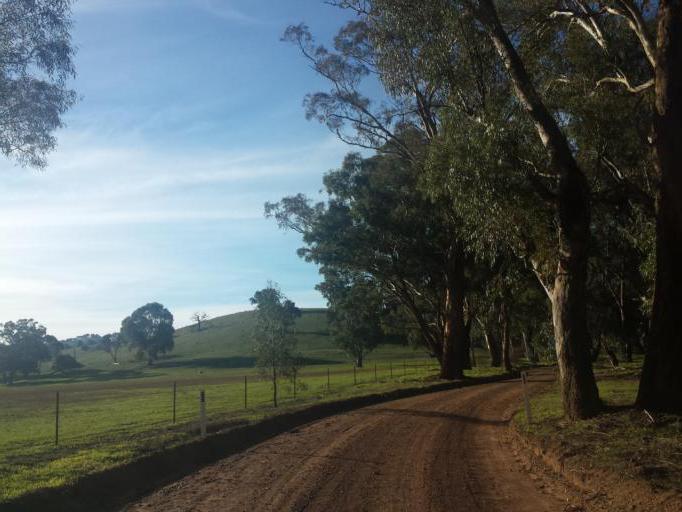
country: AU
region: Victoria
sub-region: Murrindindi
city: Kinglake West
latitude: -37.0155
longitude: 145.2169
